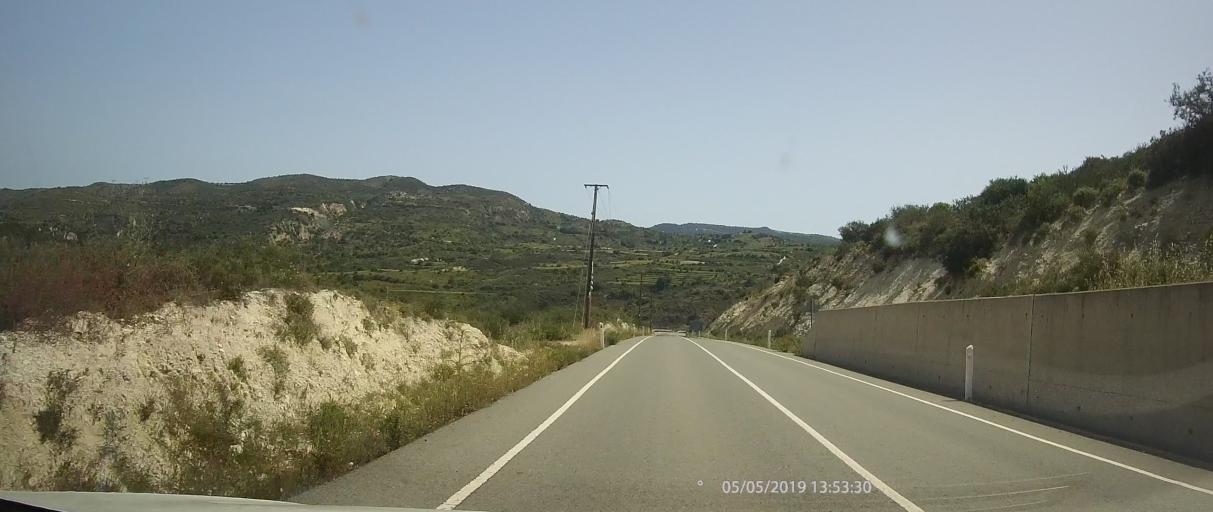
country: CY
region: Limassol
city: Pachna
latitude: 34.8198
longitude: 32.7248
